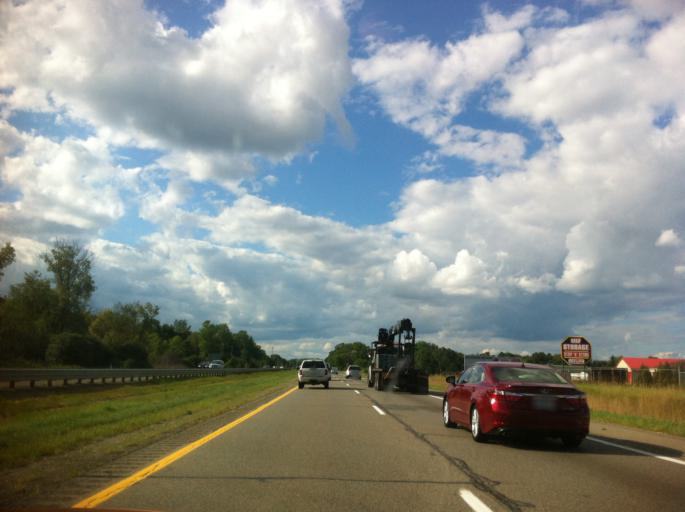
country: US
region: Michigan
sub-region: Livingston County
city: Whitmore Lake
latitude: 42.4107
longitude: -83.7635
